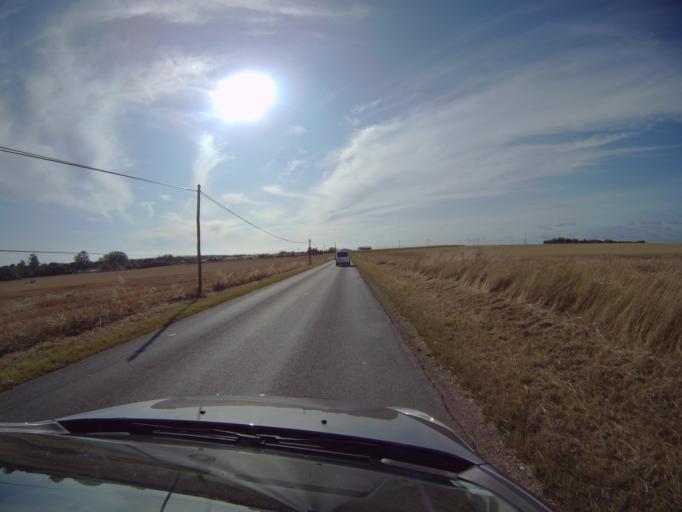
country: FR
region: Pays de la Loire
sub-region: Departement de la Vendee
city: Longeville-sur-Mer
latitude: 46.4180
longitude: -1.4600
